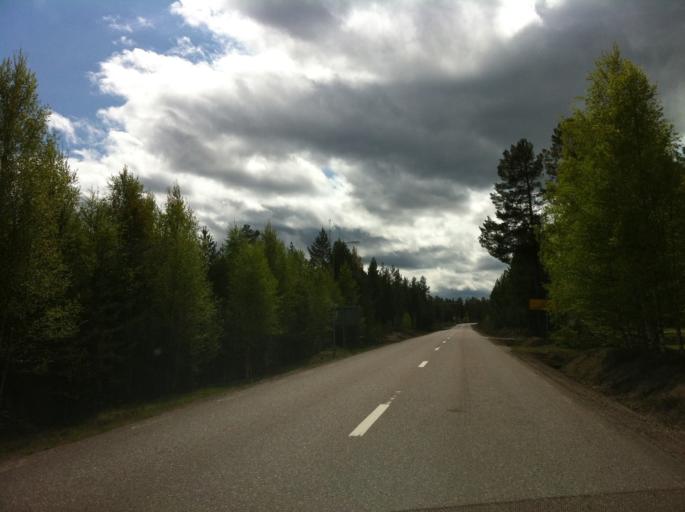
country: NO
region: Hedmark
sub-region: Trysil
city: Innbygda
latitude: 61.6844
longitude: 13.1278
